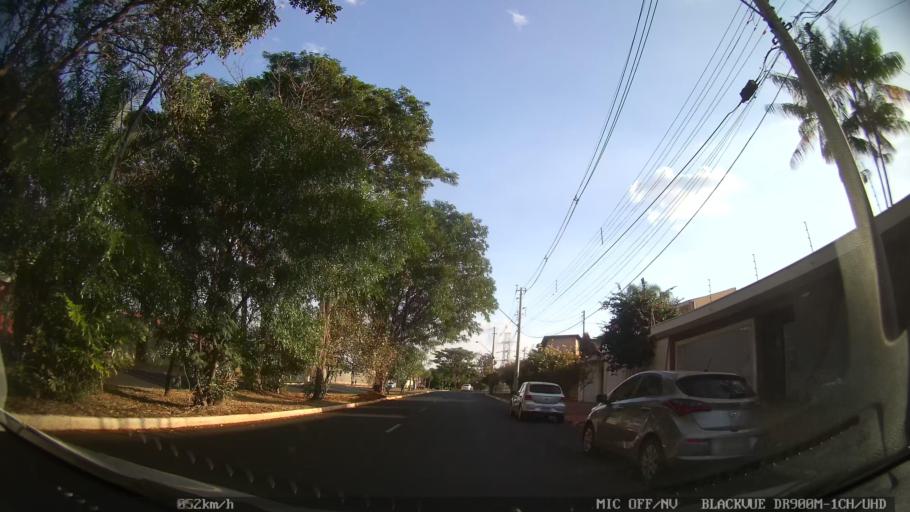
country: BR
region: Sao Paulo
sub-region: Ribeirao Preto
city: Ribeirao Preto
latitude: -21.1594
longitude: -47.8406
